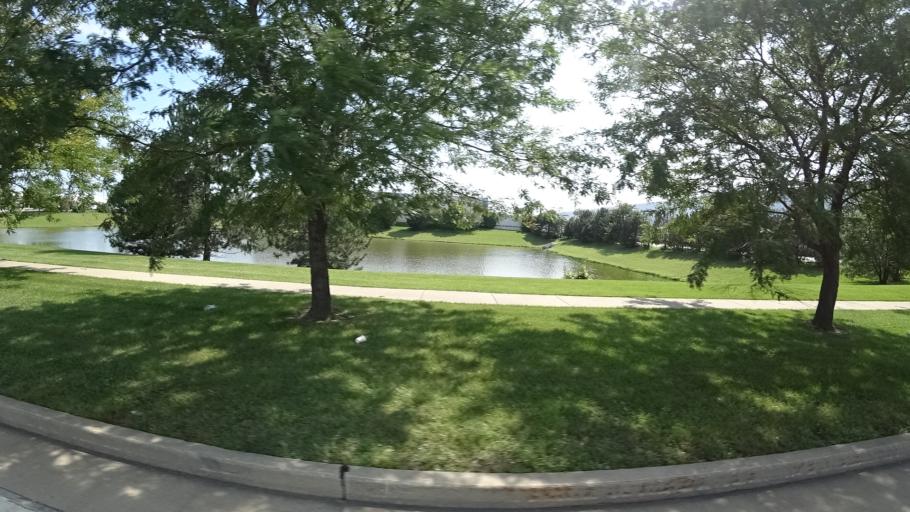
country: US
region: Illinois
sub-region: Will County
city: Frankfort Square
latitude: 41.5432
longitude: -87.8368
